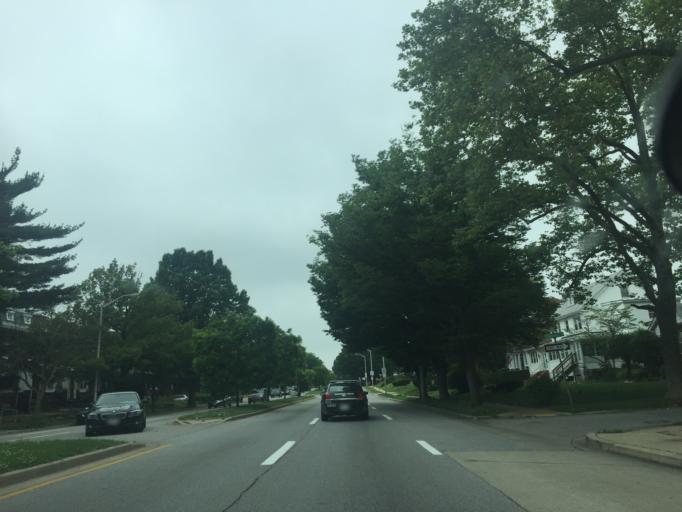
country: US
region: Maryland
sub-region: Baltimore County
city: Lochearn
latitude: 39.3253
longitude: -76.6754
